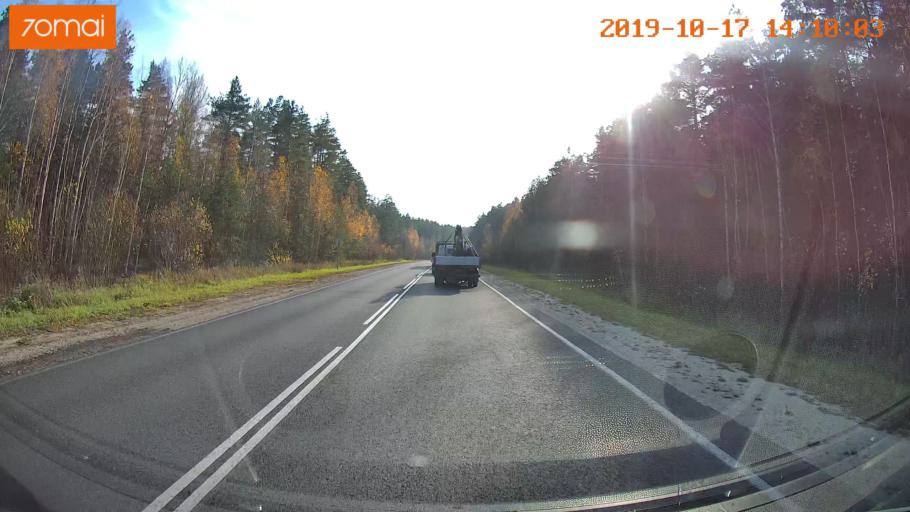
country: RU
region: Rjazan
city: Spas-Klepiki
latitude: 55.0830
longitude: 40.0528
